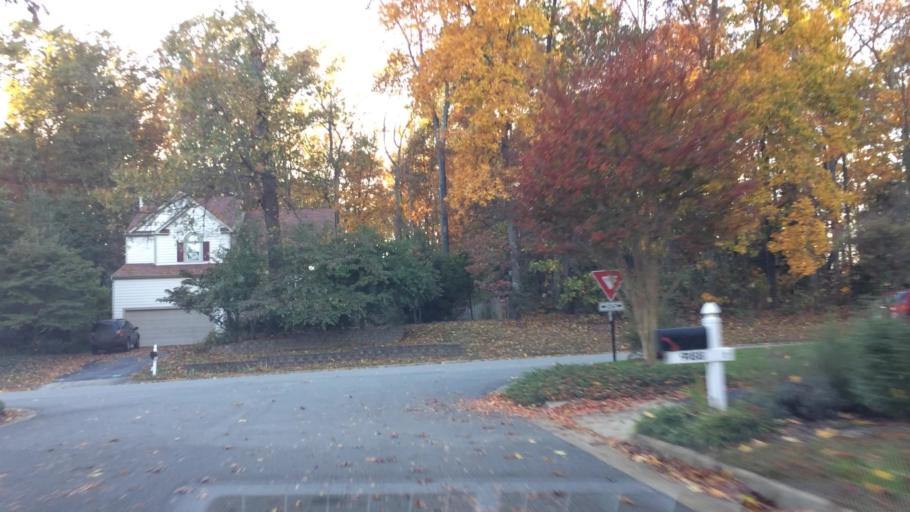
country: US
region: Virginia
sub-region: Henrico County
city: Chamberlayne
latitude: 37.6886
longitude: -77.4170
